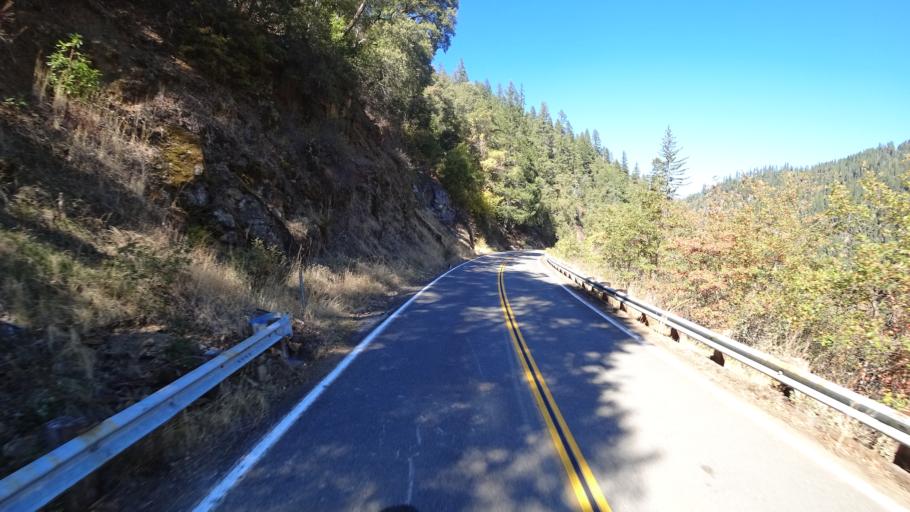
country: US
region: California
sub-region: Siskiyou County
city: Happy Camp
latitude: 41.3619
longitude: -123.4153
